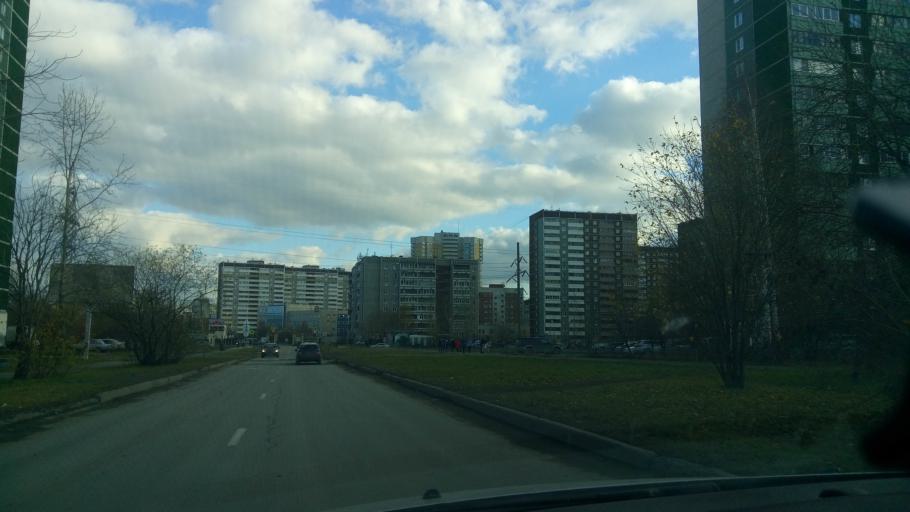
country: RU
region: Sverdlovsk
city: Yekaterinburg
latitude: 56.8661
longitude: 60.5406
